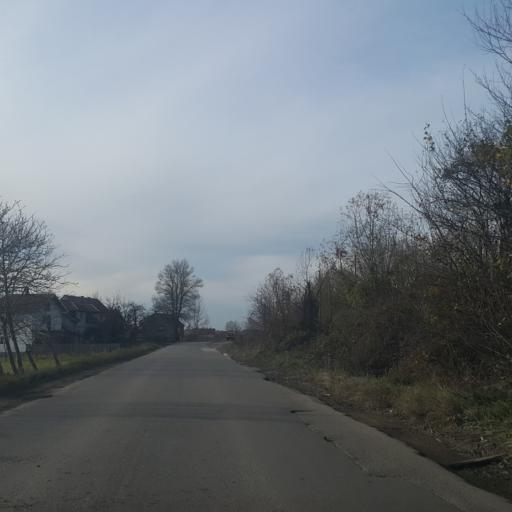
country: RS
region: Central Serbia
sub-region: Belgrade
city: Lazarevac
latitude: 44.3945
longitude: 20.3826
